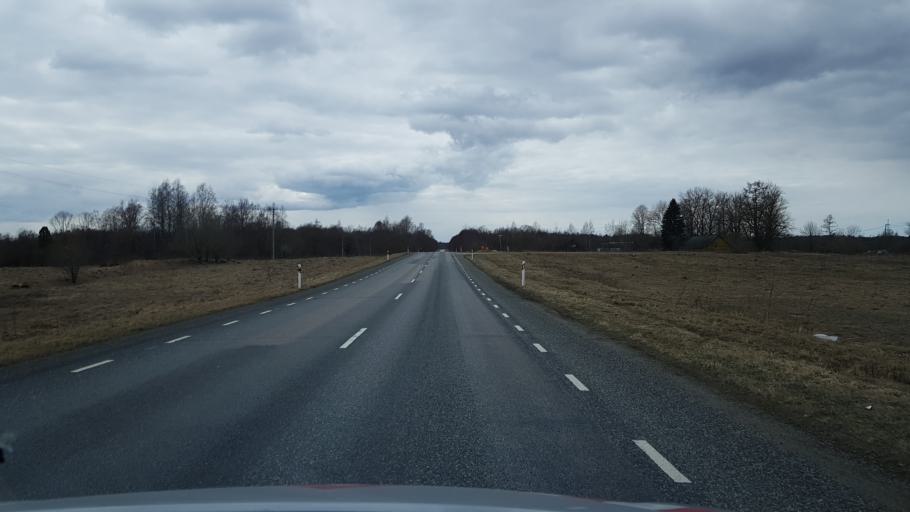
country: EE
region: Ida-Virumaa
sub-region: Narva-Joesuu linn
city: Narva-Joesuu
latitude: 59.3483
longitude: 28.0256
